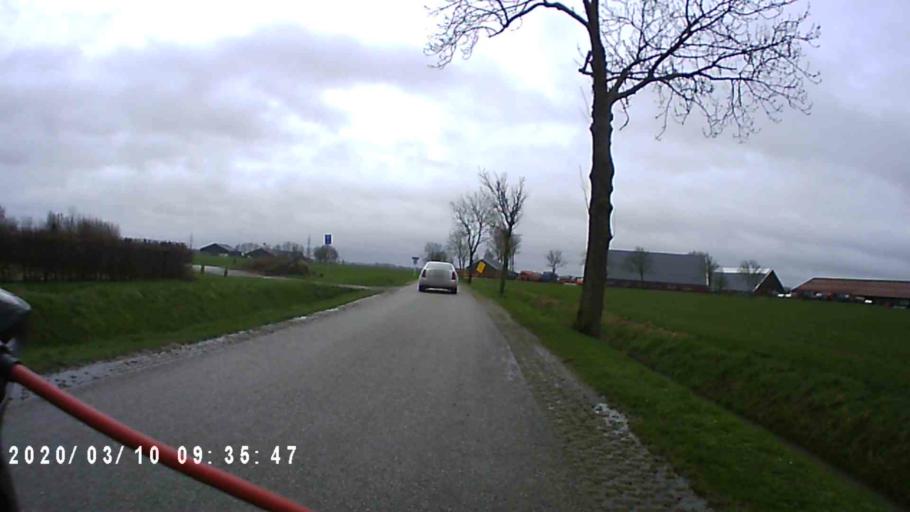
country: NL
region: Groningen
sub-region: Gemeente Winsum
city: Winsum
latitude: 53.3023
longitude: 6.4928
